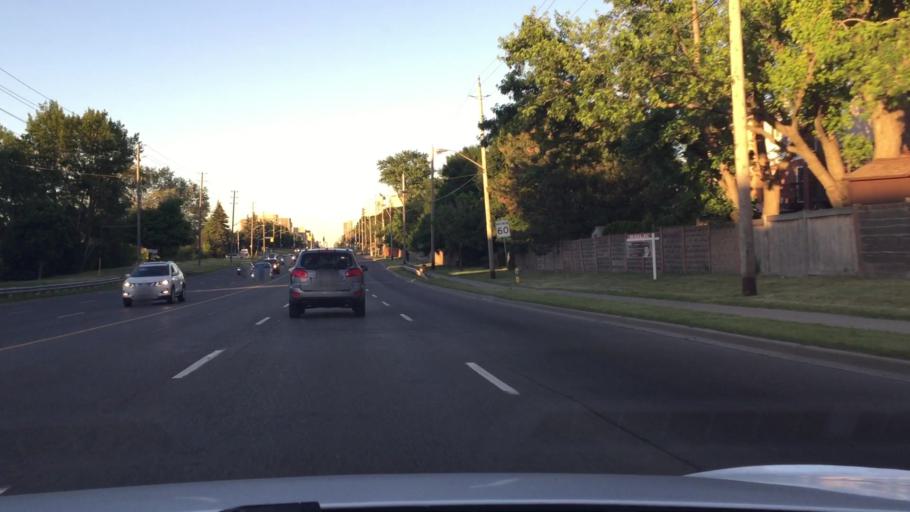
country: CA
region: Ontario
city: Concord
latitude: 43.7891
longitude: -79.4609
